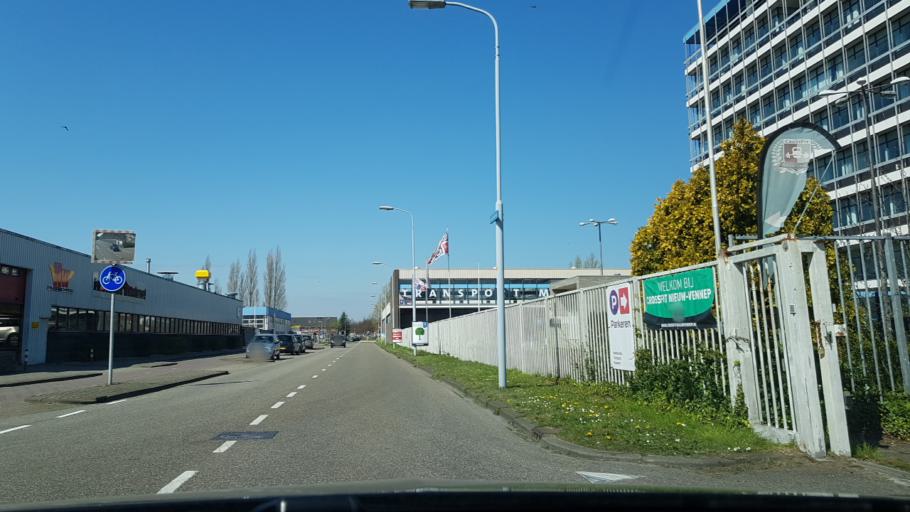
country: NL
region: South Holland
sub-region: Gemeente Hillegom
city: Hillegom
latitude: 52.2729
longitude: 4.6294
